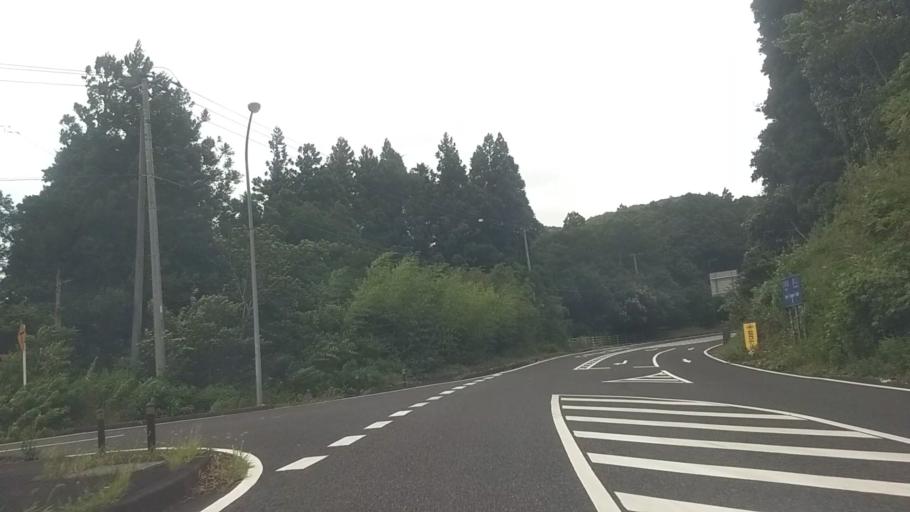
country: JP
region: Chiba
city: Kawaguchi
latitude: 35.2236
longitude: 140.0213
